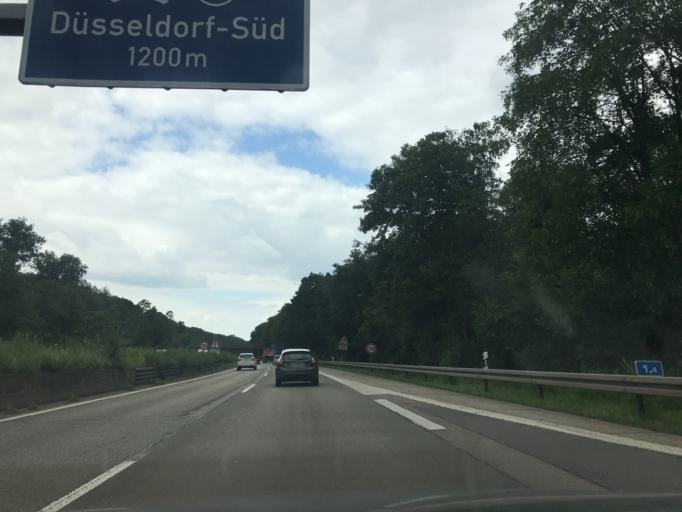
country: DE
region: North Rhine-Westphalia
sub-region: Regierungsbezirk Dusseldorf
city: Erkrath
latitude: 51.1798
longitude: 6.8822
